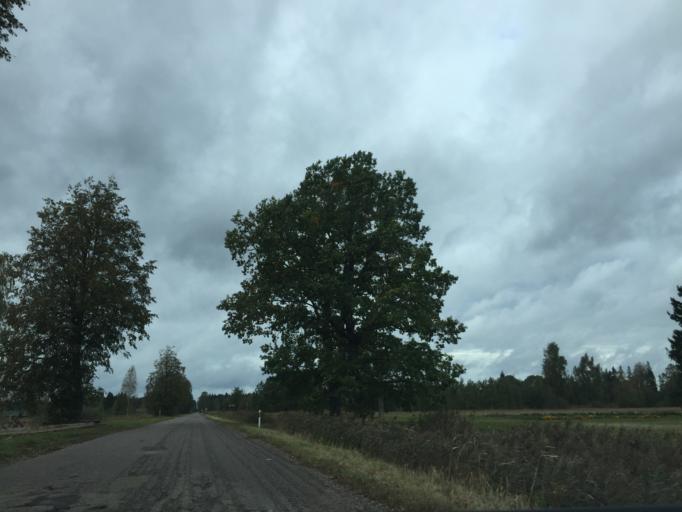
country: LV
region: Olaine
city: Olaine
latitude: 56.7672
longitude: 23.8799
